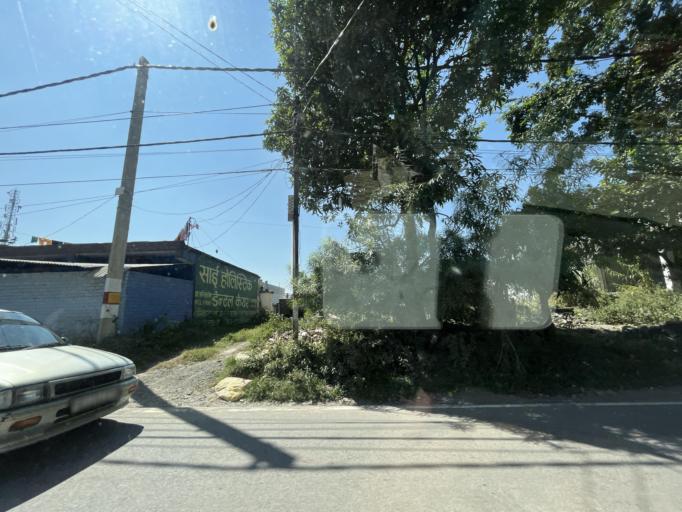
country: IN
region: Uttarakhand
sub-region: Naini Tal
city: Kaladhungi
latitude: 29.2866
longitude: 79.3457
